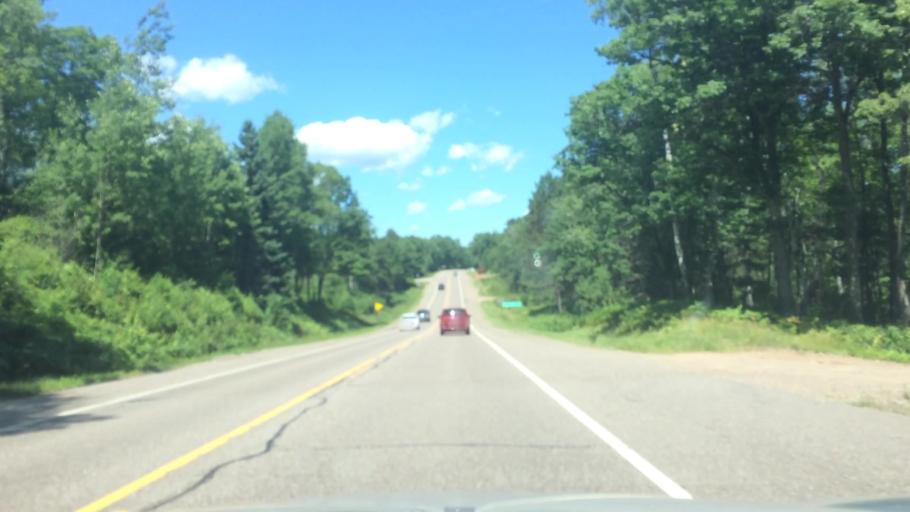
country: US
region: Wisconsin
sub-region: Vilas County
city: Lac du Flambeau
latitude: 45.7756
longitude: -89.7155
